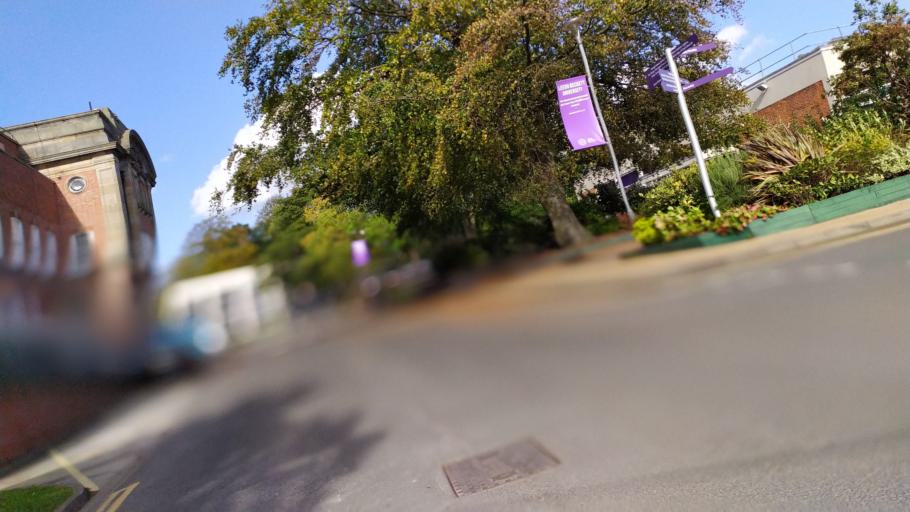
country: GB
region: England
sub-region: City and Borough of Leeds
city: Horsforth
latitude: 53.8272
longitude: -1.5922
